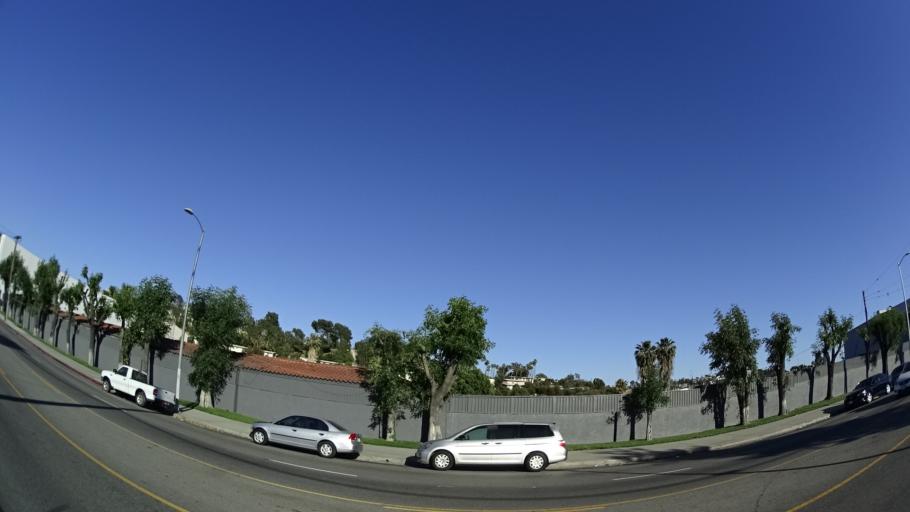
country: US
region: California
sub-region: Los Angeles County
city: Belvedere
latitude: 34.0642
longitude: -118.1813
